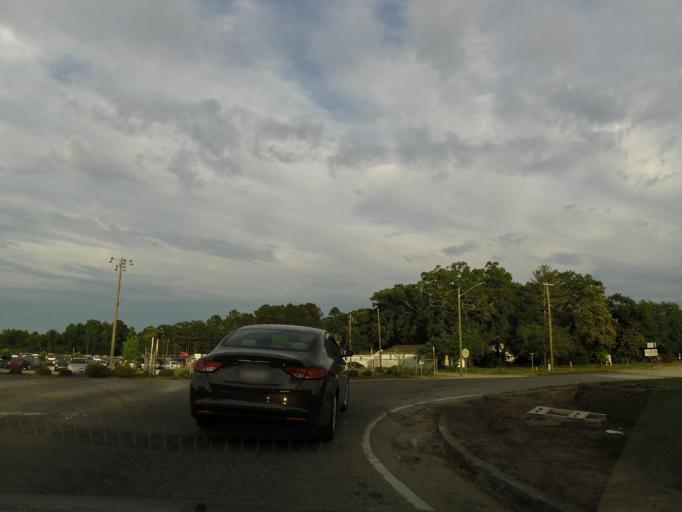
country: US
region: Georgia
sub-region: Chatham County
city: Garden City
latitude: 32.0860
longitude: -81.1976
